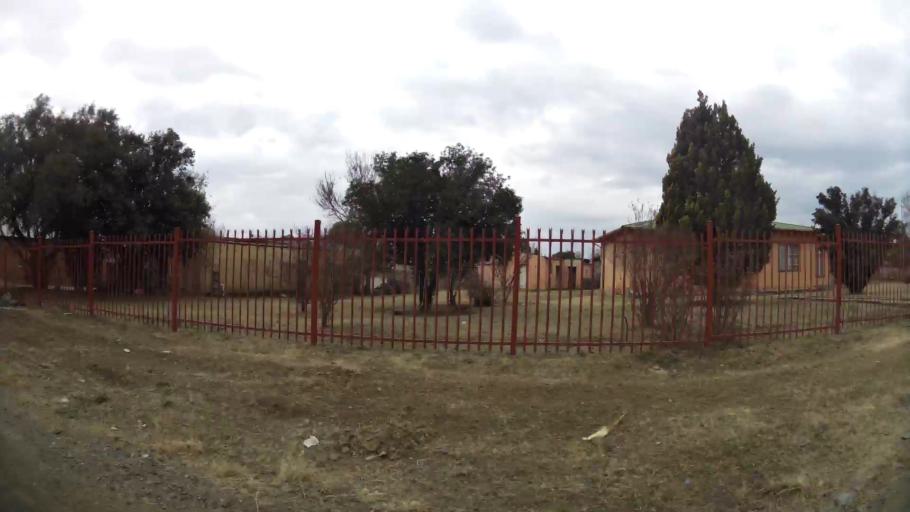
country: ZA
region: Orange Free State
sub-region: Fezile Dabi District Municipality
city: Kroonstad
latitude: -27.6784
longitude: 27.2333
